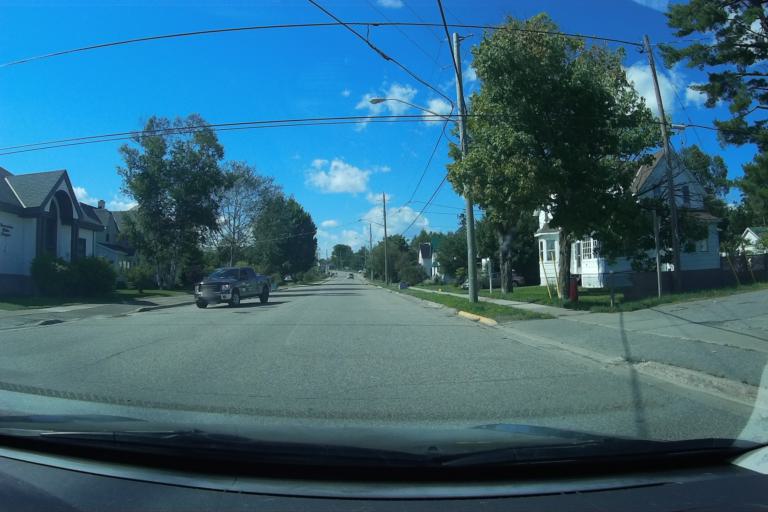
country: CA
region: Ontario
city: Thessalon
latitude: 46.2565
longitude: -83.5574
